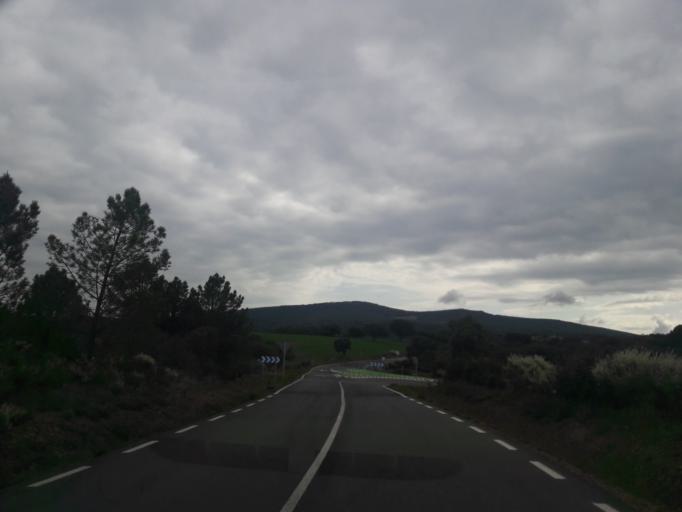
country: ES
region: Castille and Leon
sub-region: Provincia de Salamanca
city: Zamarra
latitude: 40.5448
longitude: -6.4210
